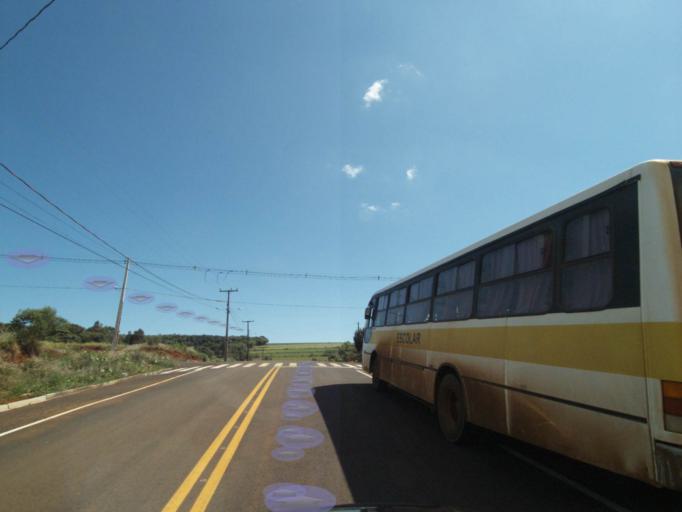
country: BR
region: Parana
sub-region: Coronel Vivida
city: Coronel Vivida
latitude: -26.1468
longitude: -52.3824
